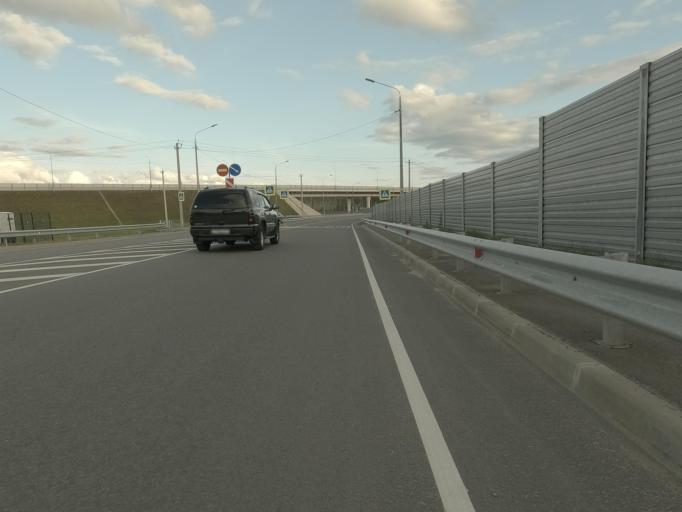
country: RU
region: Leningrad
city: Mga
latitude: 59.7572
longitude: 31.0901
